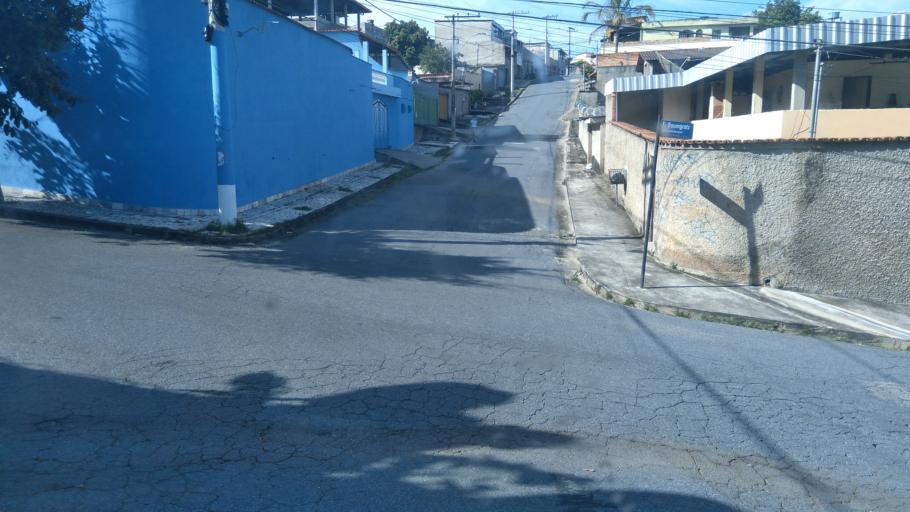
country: BR
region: Minas Gerais
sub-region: Belo Horizonte
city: Belo Horizonte
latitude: -19.8625
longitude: -43.9012
